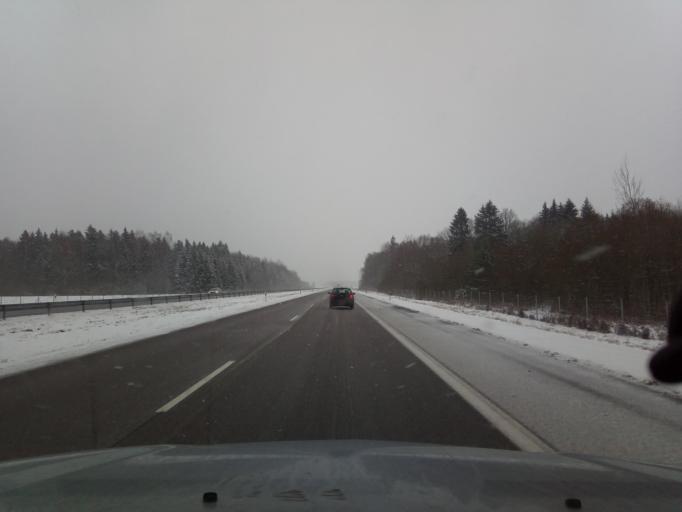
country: LT
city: Sirvintos
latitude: 54.9945
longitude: 24.9276
